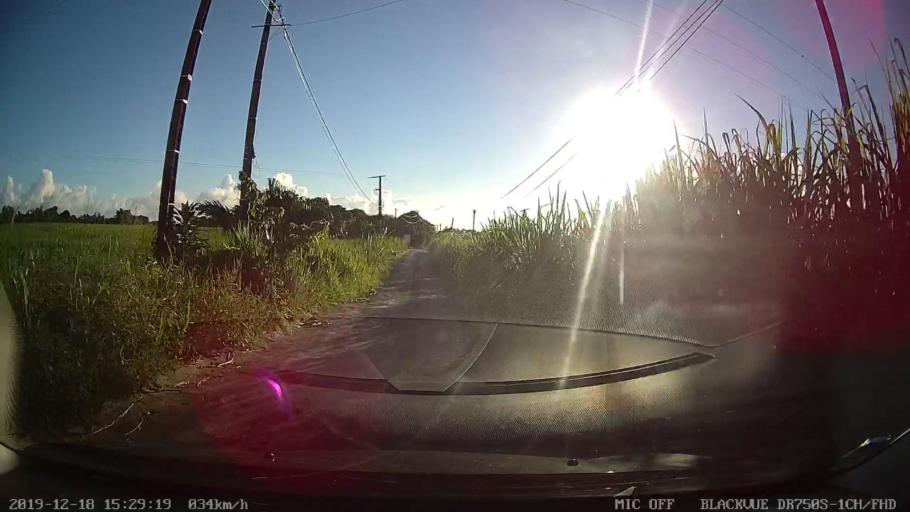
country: RE
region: Reunion
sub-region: Reunion
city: Bras-Panon
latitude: -20.9987
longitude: 55.6608
